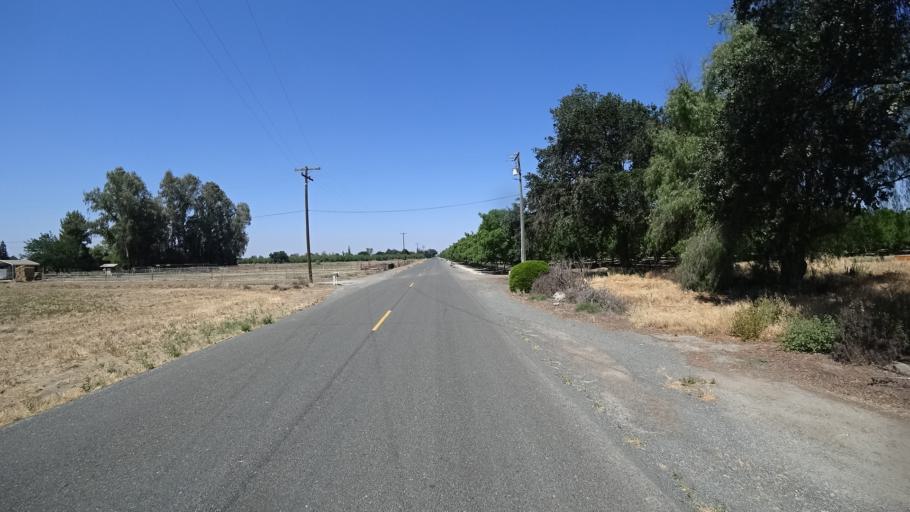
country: US
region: California
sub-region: Fresno County
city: Laton
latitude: 36.4307
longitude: -119.6225
